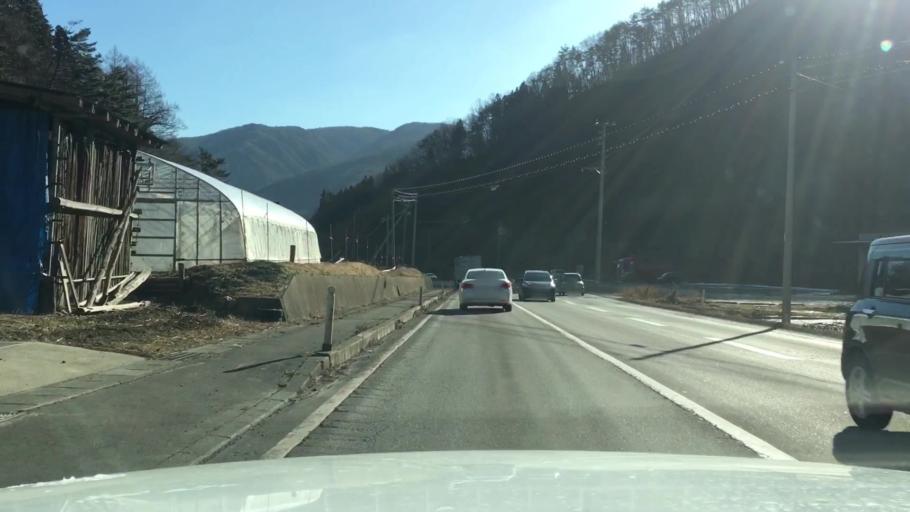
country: JP
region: Iwate
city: Miyako
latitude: 39.5973
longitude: 141.6493
